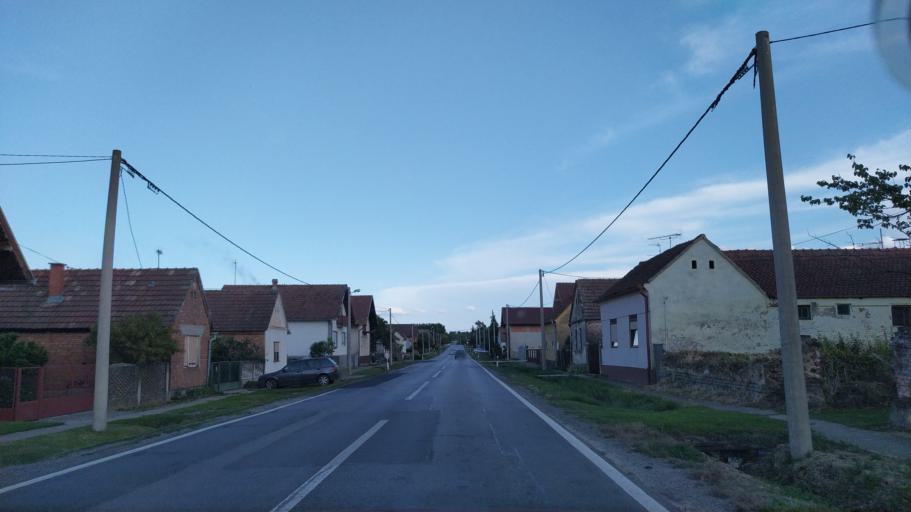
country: HR
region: Virovitick-Podravska
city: Slatina
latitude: 45.7300
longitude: 17.6275
